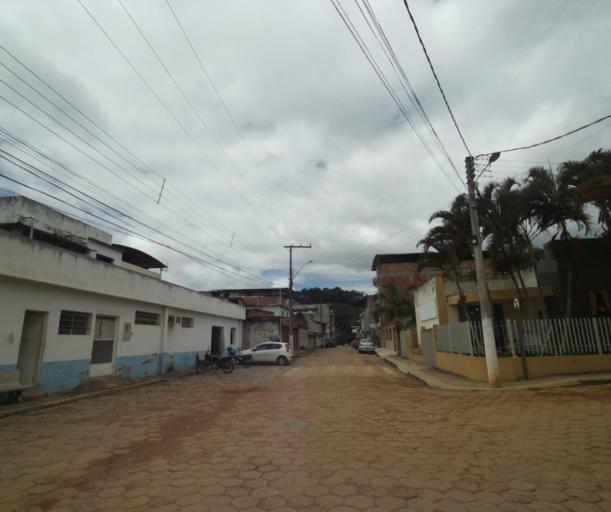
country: BR
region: Espirito Santo
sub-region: Irupi
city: Irupi
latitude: -20.3483
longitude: -41.6381
